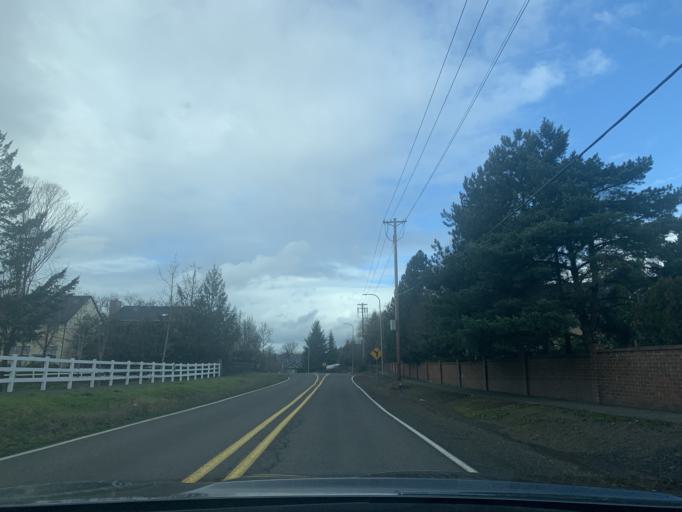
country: US
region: Oregon
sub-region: Washington County
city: Oak Hills
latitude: 45.5584
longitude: -122.8314
